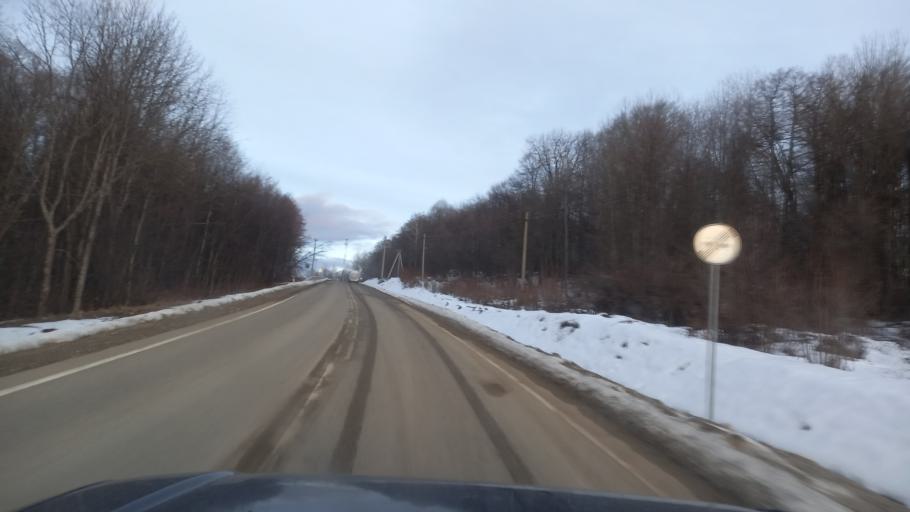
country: RU
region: Adygeya
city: Kamennomostskiy
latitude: 44.2208
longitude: 39.9872
